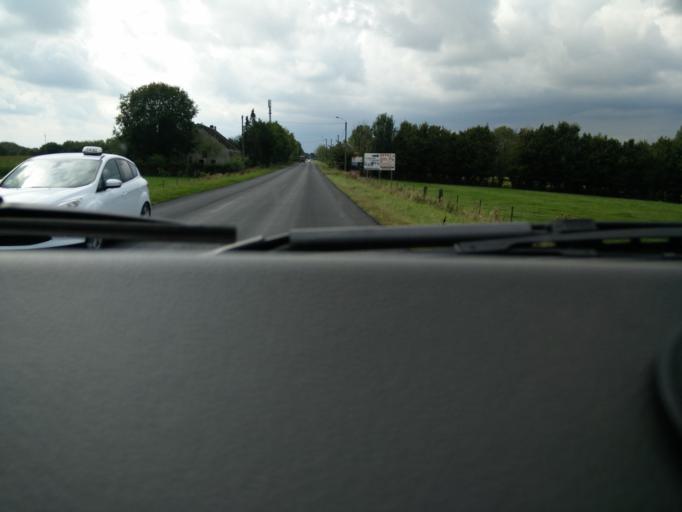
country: FR
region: Champagne-Ardenne
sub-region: Departement des Ardennes
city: Signy-le-Petit
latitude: 49.8721
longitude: 4.3618
